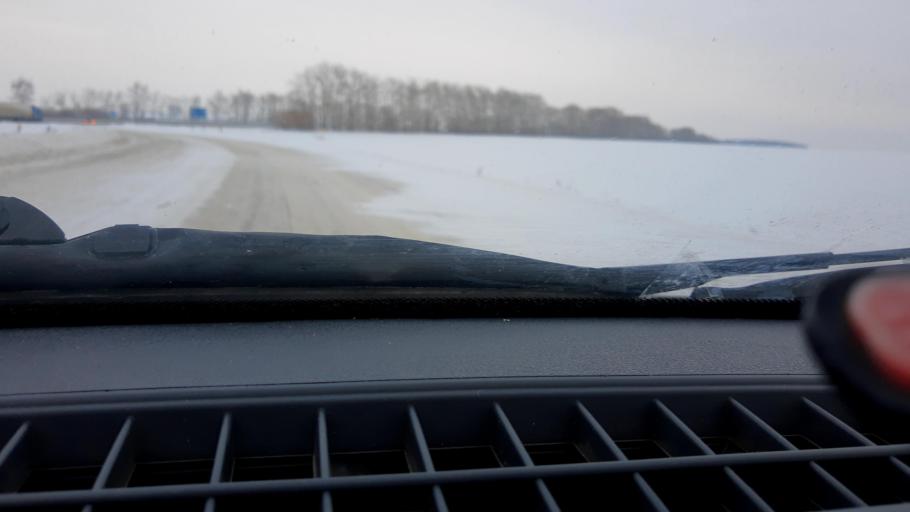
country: RU
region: Bashkortostan
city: Alekseyevka
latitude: 54.7296
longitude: 55.0326
